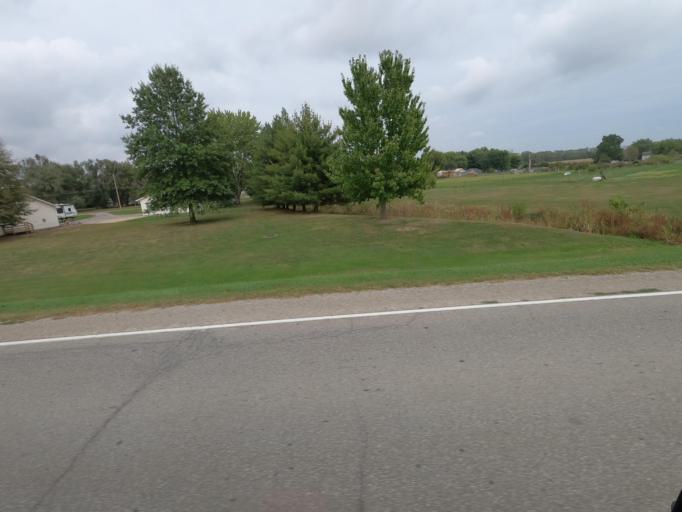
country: US
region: Iowa
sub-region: Wapello County
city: Ottumwa
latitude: 40.9139
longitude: -92.2149
